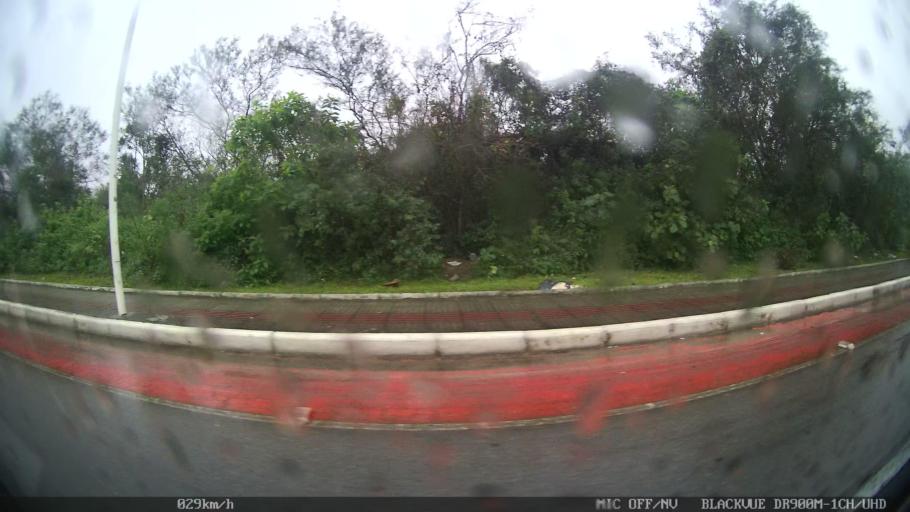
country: BR
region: Santa Catarina
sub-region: Itajai
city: Itajai
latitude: -26.9183
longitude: -48.6857
